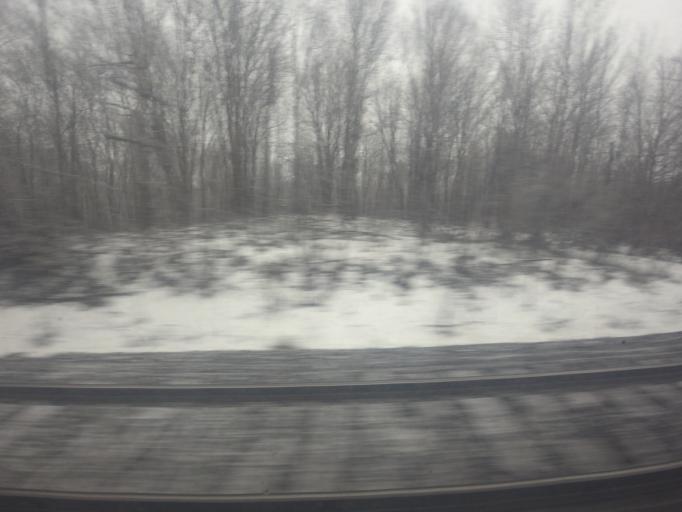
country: CA
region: Ontario
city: Brockville
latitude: 44.5759
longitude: -75.7412
